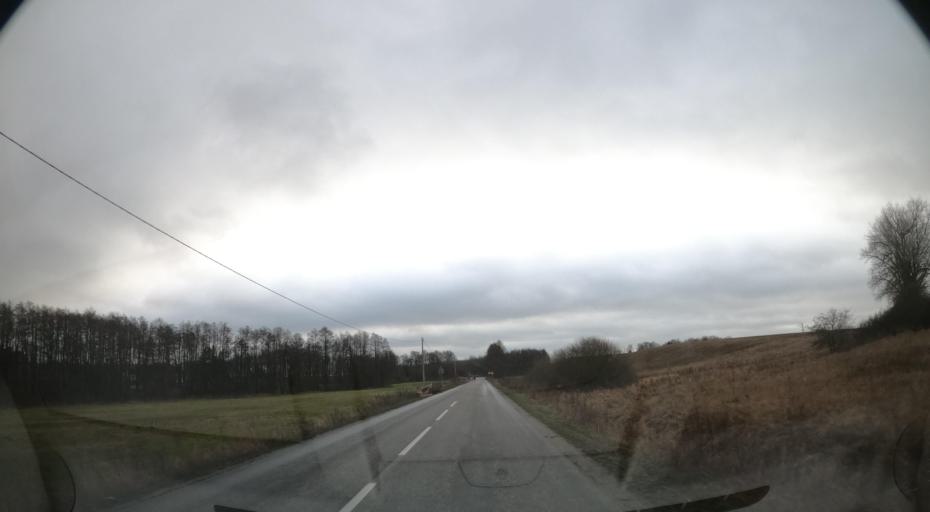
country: PL
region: Kujawsko-Pomorskie
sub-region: Powiat nakielski
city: Sadki
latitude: 53.1901
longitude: 17.3940
